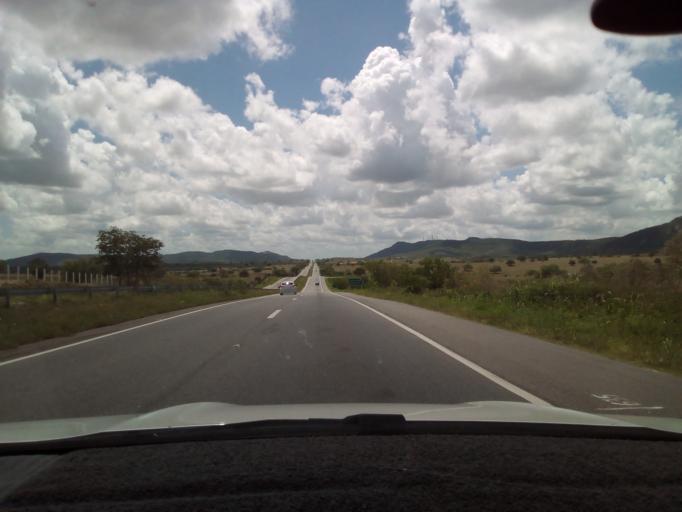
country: BR
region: Paraiba
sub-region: Gurinhem
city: Gurinhem
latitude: -7.1913
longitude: -35.4717
